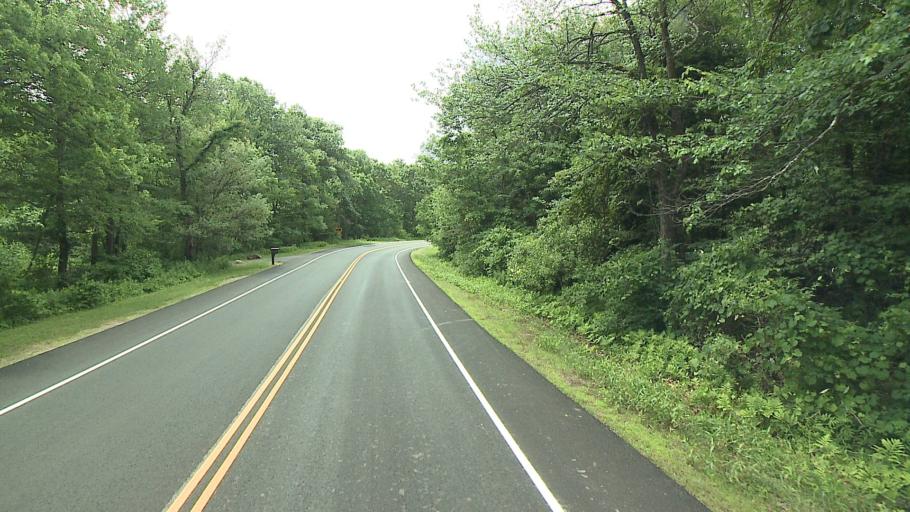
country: US
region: Connecticut
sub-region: Hartford County
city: North Granby
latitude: 42.0004
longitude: -72.8971
